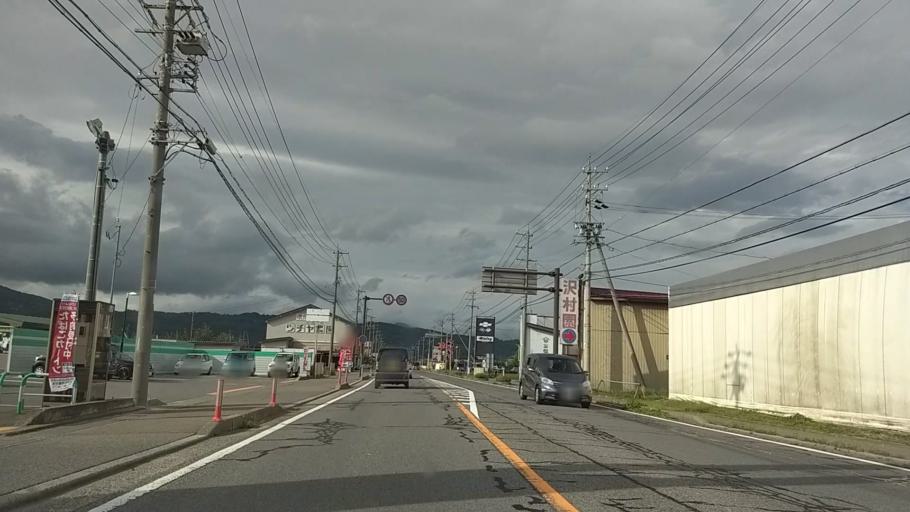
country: JP
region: Nagano
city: Suzaka
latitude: 36.6835
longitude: 138.2678
